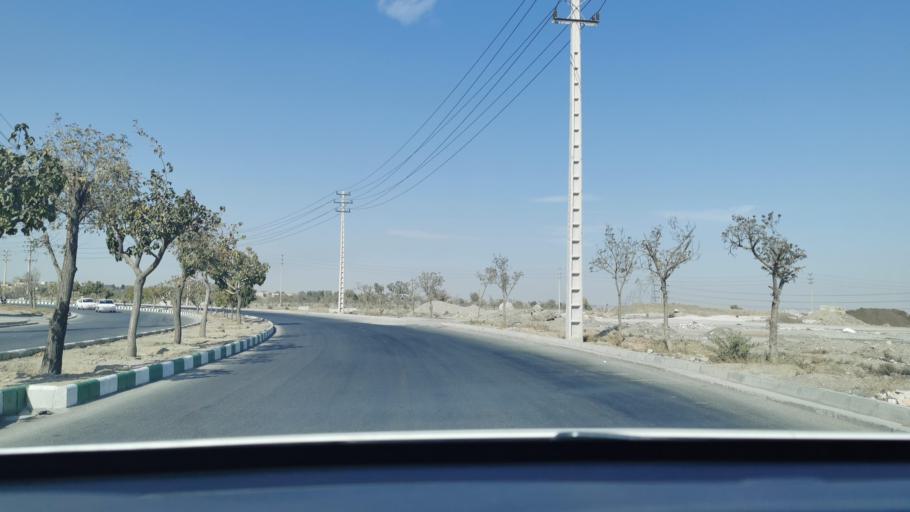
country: IR
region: Razavi Khorasan
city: Mashhad
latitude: 36.3466
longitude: 59.6116
